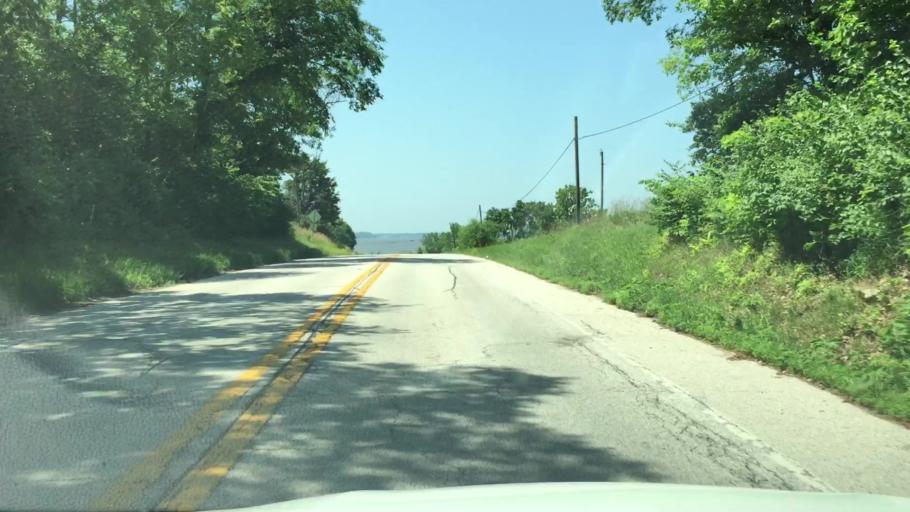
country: US
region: Illinois
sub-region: Hancock County
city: Nauvoo
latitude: 40.5154
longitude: -91.3592
